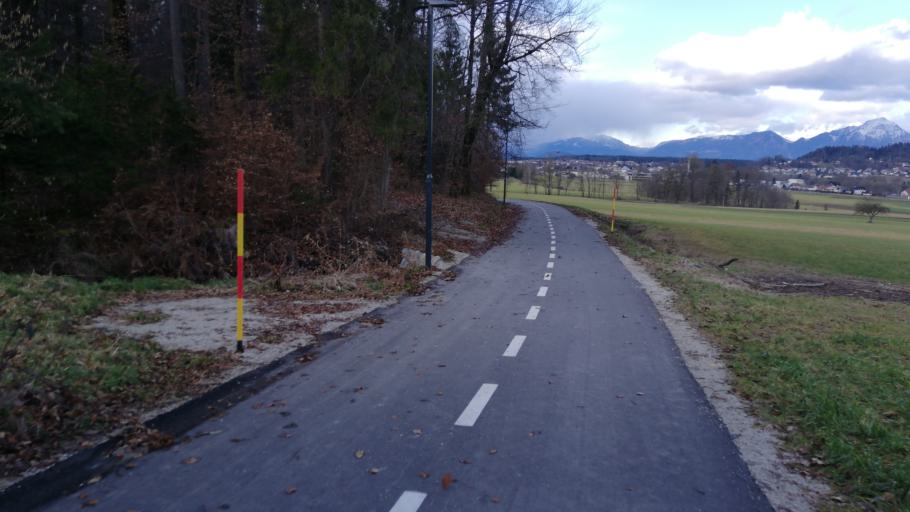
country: SI
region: Medvode
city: Medvode
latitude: 46.1229
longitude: 14.4214
